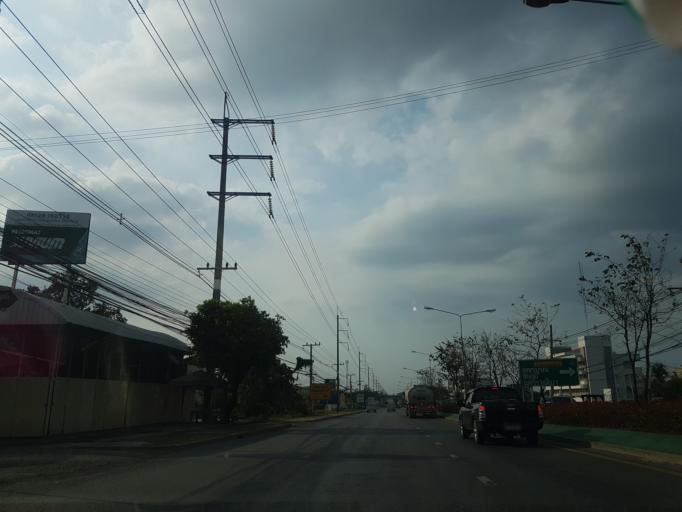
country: TH
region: Sara Buri
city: Phra Phutthabat
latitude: 14.7330
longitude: 100.7812
